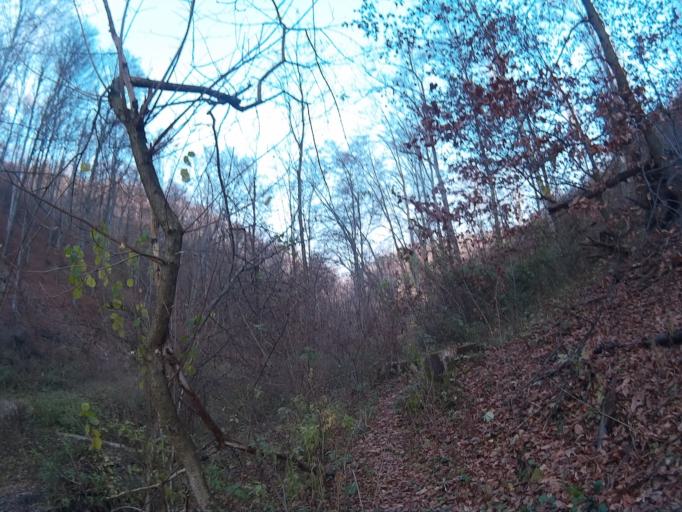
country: HU
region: Heves
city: Szilvasvarad
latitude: 48.0725
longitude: 20.4056
